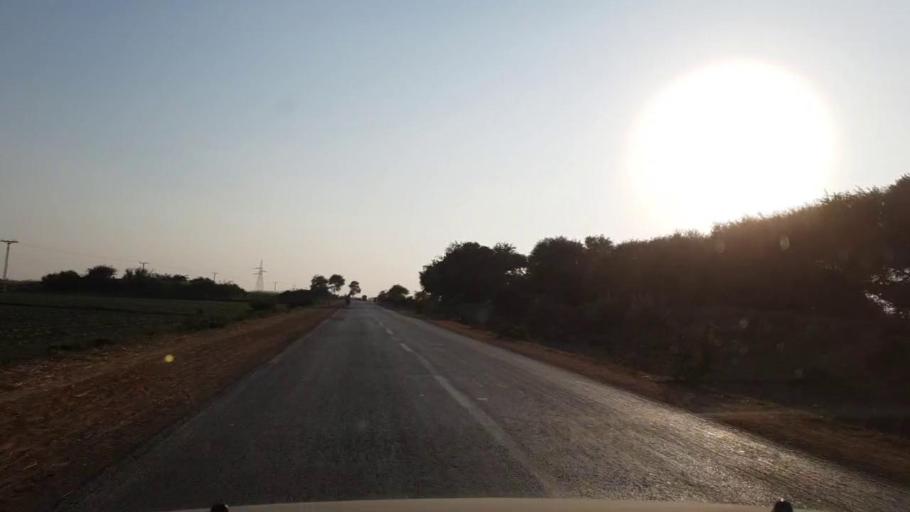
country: PK
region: Sindh
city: Daro Mehar
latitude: 24.6555
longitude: 68.1296
